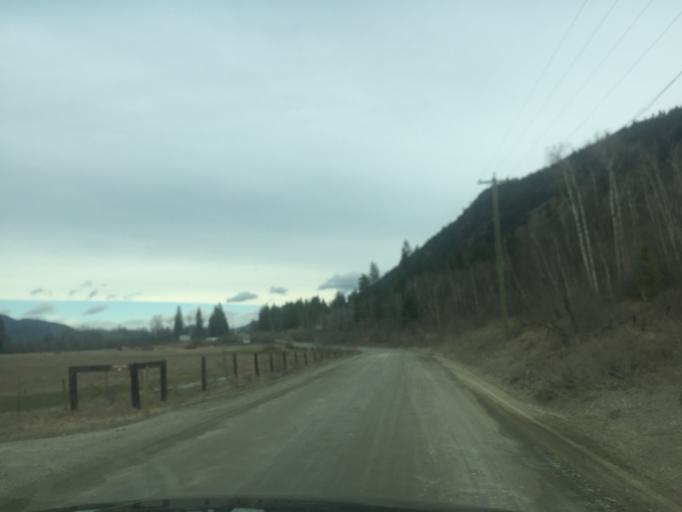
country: CA
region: British Columbia
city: Kamloops
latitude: 51.2676
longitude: -120.1518
